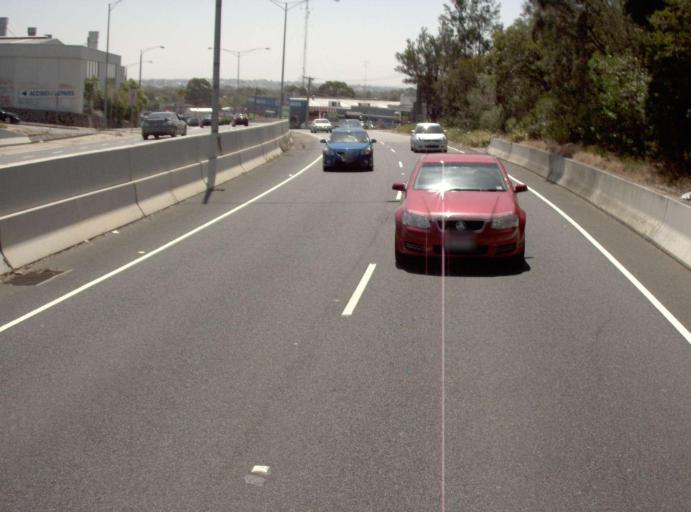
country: AU
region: Victoria
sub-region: Banyule
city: Heidelberg Heights
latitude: -37.7551
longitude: 145.0553
